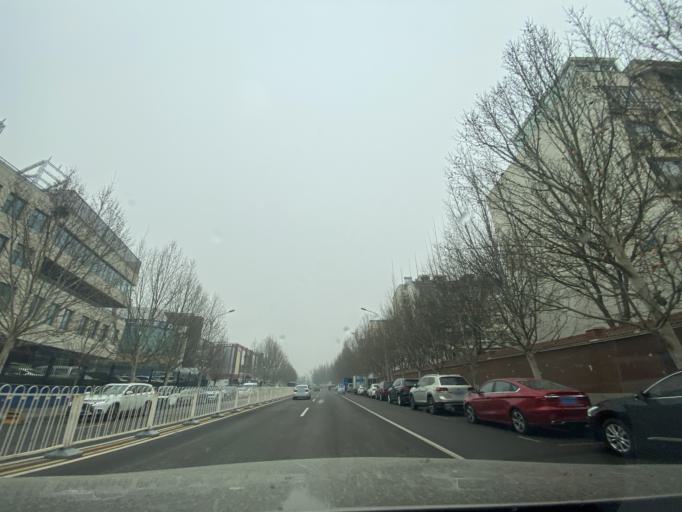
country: CN
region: Beijing
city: Sijiqing
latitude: 39.9645
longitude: 116.2417
